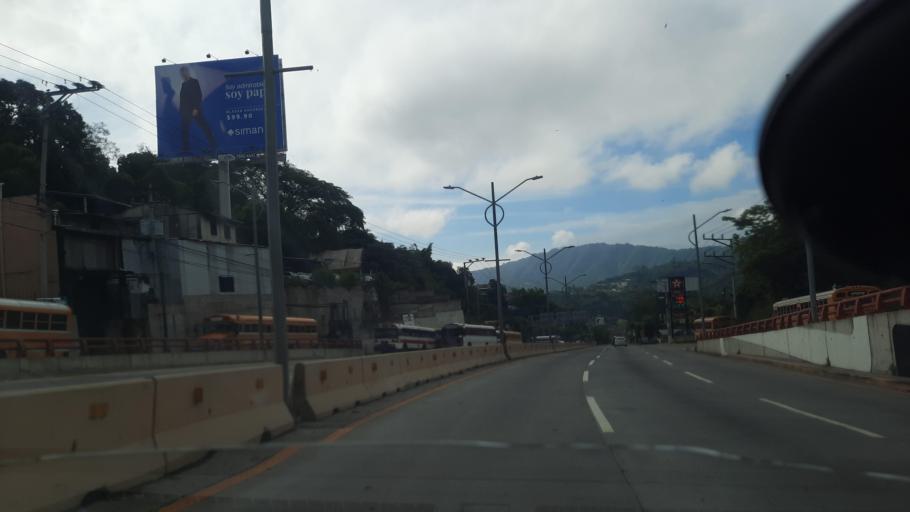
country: SV
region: San Salvador
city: San Salvador
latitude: 13.6788
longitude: -89.2087
